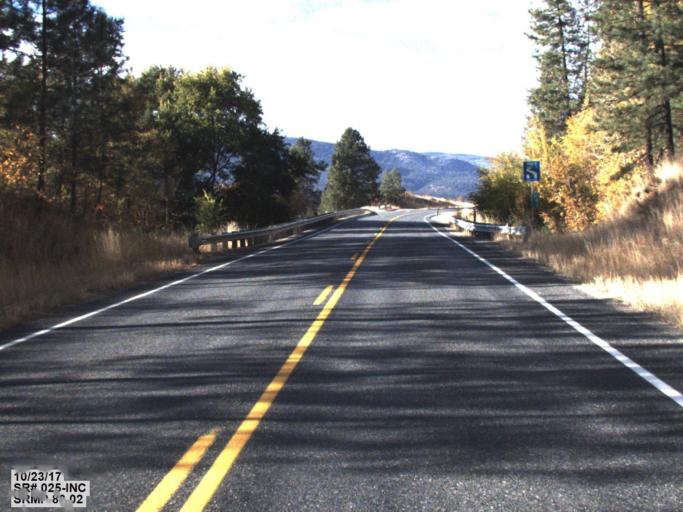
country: US
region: Washington
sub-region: Stevens County
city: Kettle Falls
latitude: 48.6311
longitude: -118.0783
